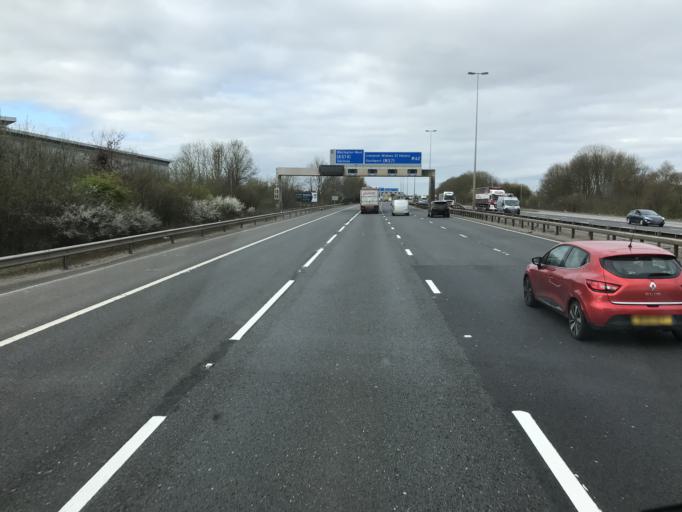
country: GB
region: England
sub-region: Warrington
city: Great Sankey
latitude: 53.4177
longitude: -2.6323
